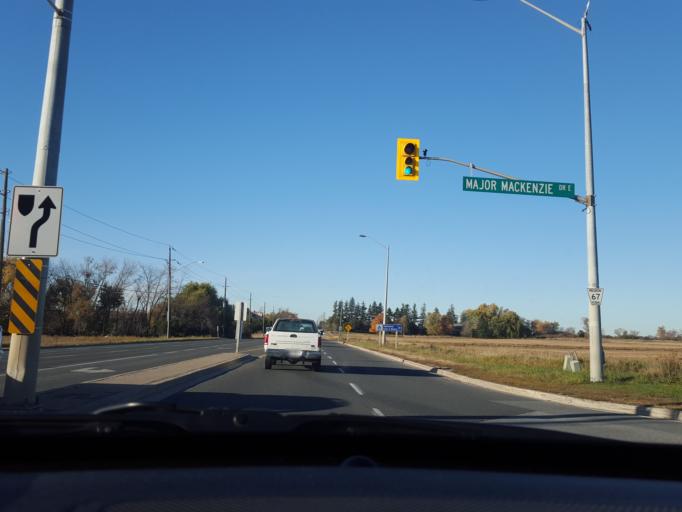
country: CA
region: Ontario
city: Markham
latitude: 43.9037
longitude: -79.2932
